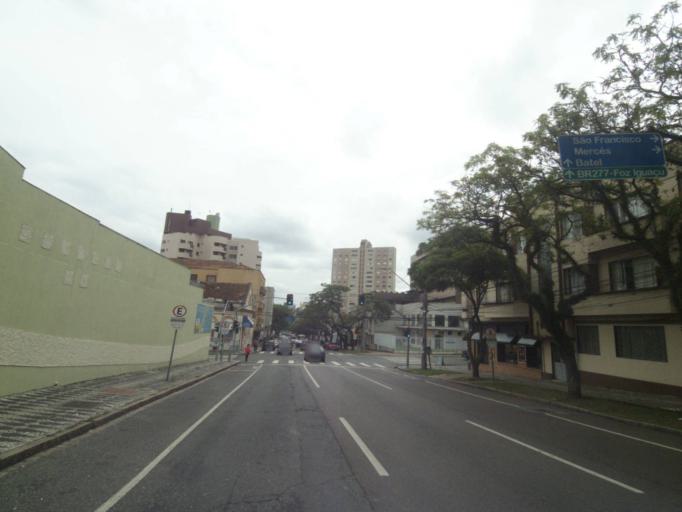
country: BR
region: Parana
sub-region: Curitiba
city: Curitiba
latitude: -25.4296
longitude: -49.2776
